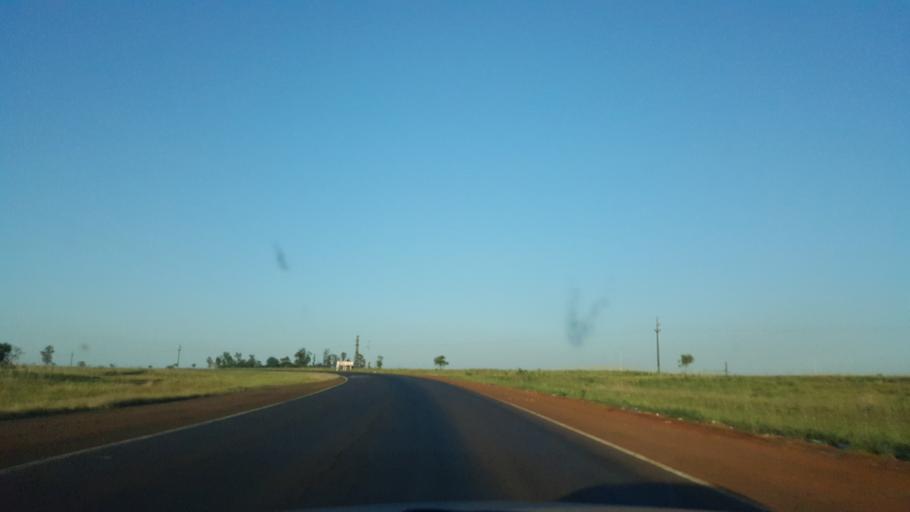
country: AR
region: Corrientes
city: Santo Tome
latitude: -28.3570
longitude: -56.1119
